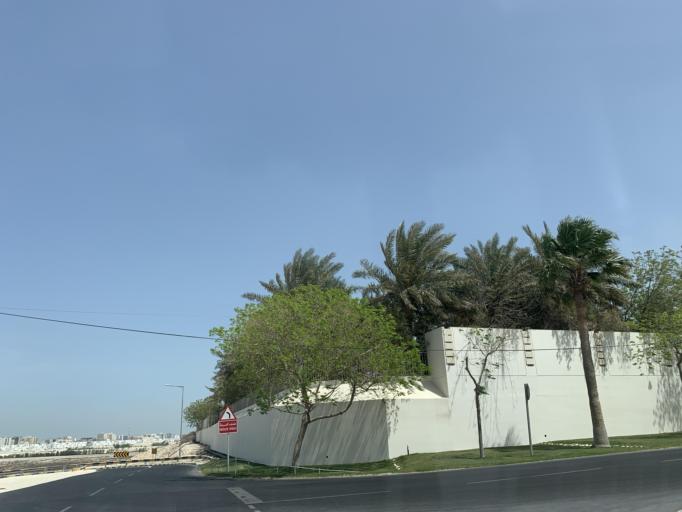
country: BH
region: Northern
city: Ar Rifa'
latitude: 26.1487
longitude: 50.5479
